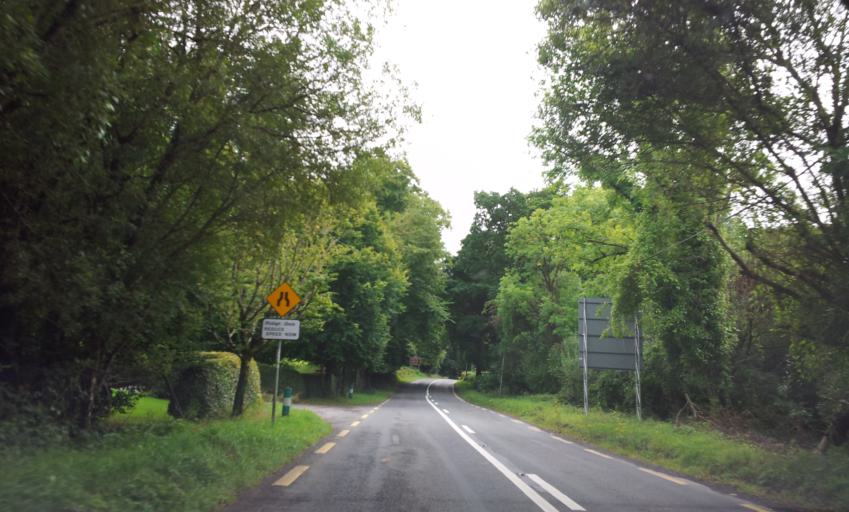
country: IE
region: Munster
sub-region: Ciarrai
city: Cill Airne
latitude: 52.0163
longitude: -9.4942
